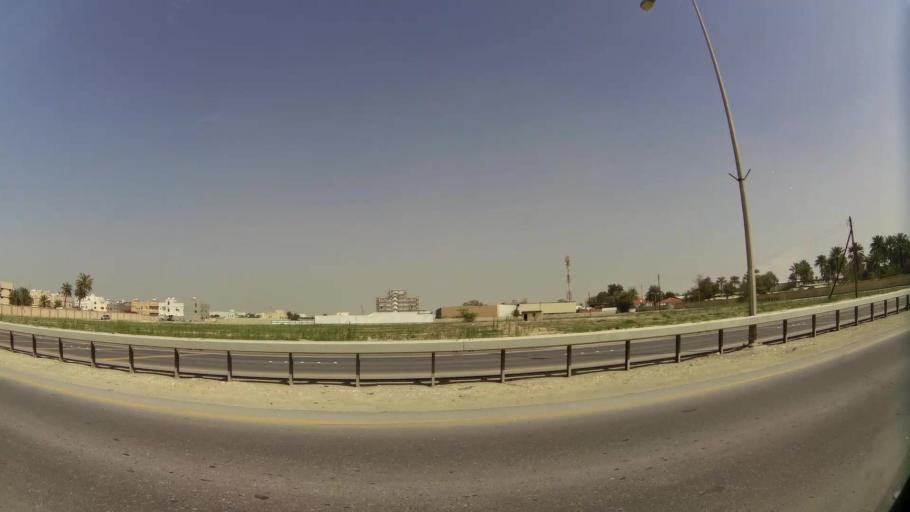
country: BH
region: Manama
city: Jidd Hafs
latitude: 26.2041
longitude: 50.4587
